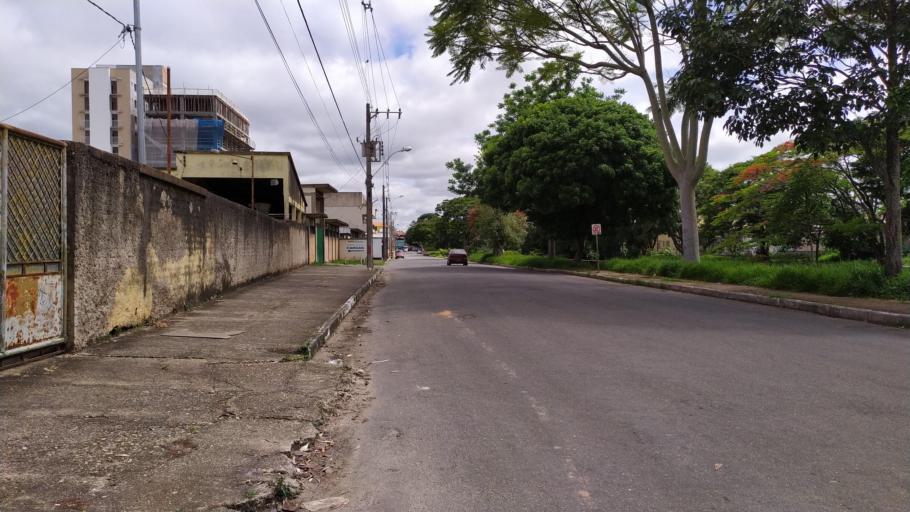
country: BR
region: Minas Gerais
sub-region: Sao Joao Del Rei
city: Sao Joao del Rei
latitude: -21.1251
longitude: -44.2459
